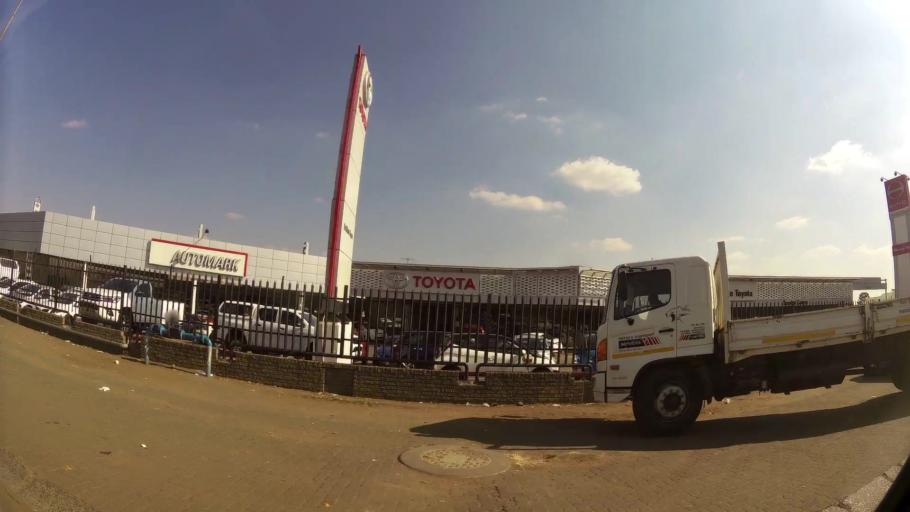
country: ZA
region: Gauteng
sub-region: Ekurhuleni Metropolitan Municipality
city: Boksburg
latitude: -26.2061
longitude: 28.2844
